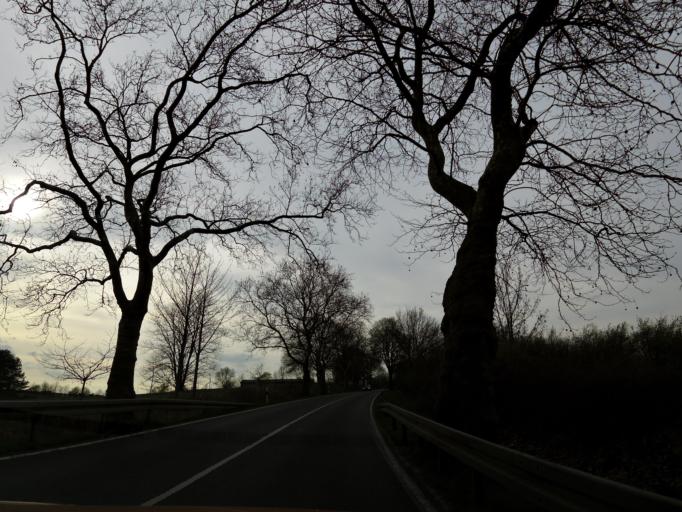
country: DE
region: Brandenburg
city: Bestensee
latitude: 52.2424
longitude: 13.6082
